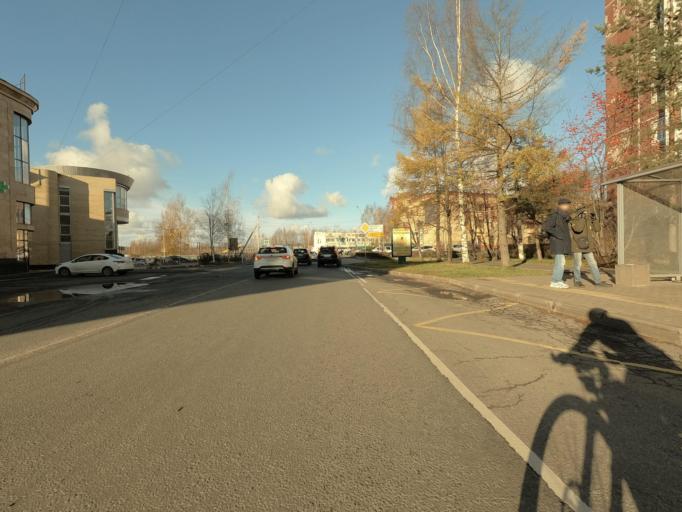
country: RU
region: Leningrad
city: Vsevolozhsk
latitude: 60.0312
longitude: 30.6294
